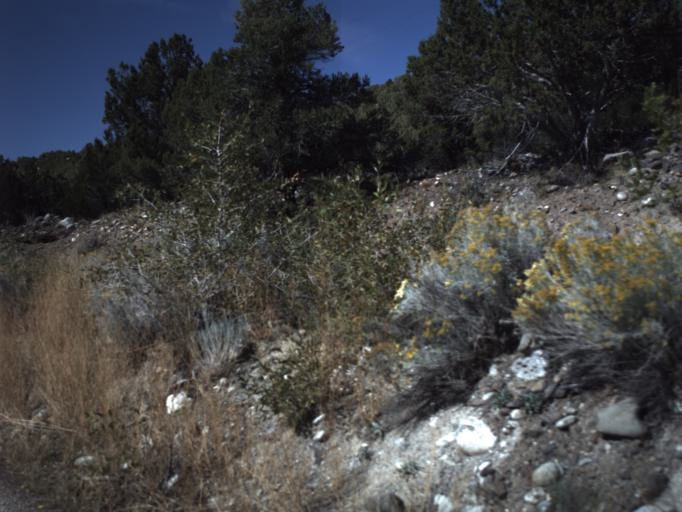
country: US
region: Utah
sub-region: Beaver County
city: Beaver
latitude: 38.2809
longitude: -112.5780
